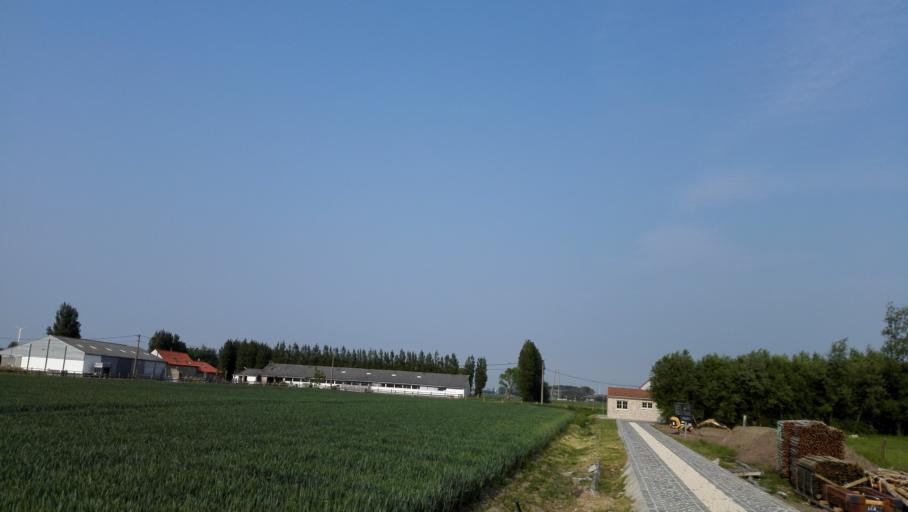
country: BE
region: Flanders
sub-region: Provincie West-Vlaanderen
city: Zuienkerke
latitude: 51.2948
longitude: 3.1623
